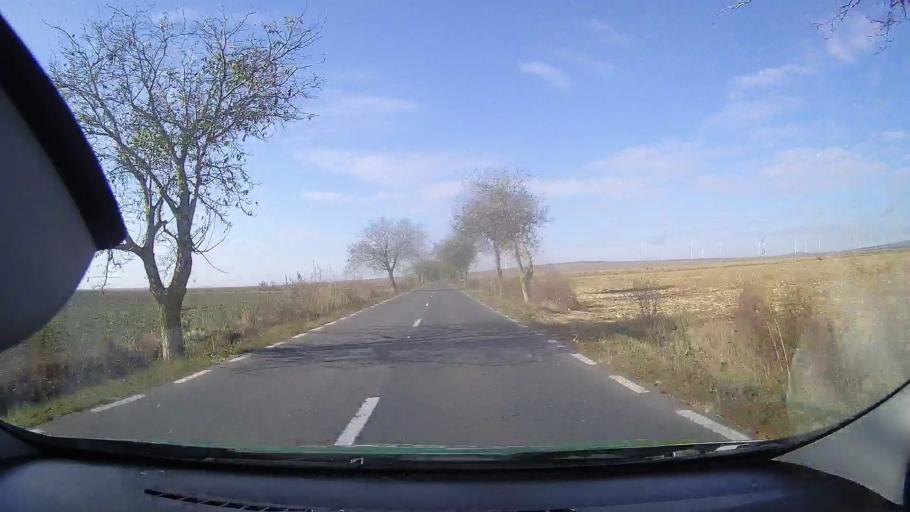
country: RO
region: Tulcea
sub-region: Comuna Bestepe
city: Bestepe
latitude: 45.0276
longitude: 29.0154
